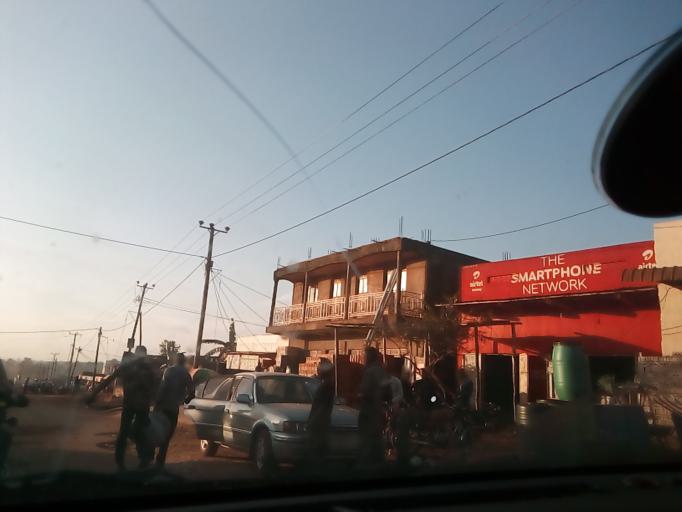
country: UG
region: Central Region
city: Masaka
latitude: -0.3210
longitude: 31.7610
